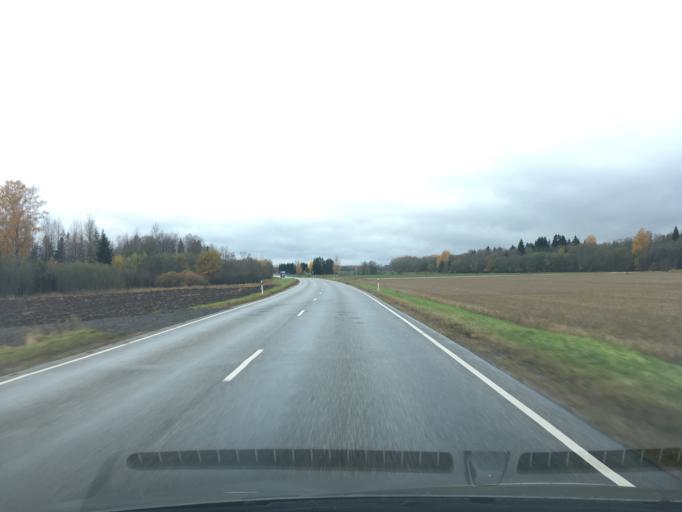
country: EE
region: Jogevamaa
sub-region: Tabivere vald
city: Tabivere
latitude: 58.4632
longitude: 26.5515
